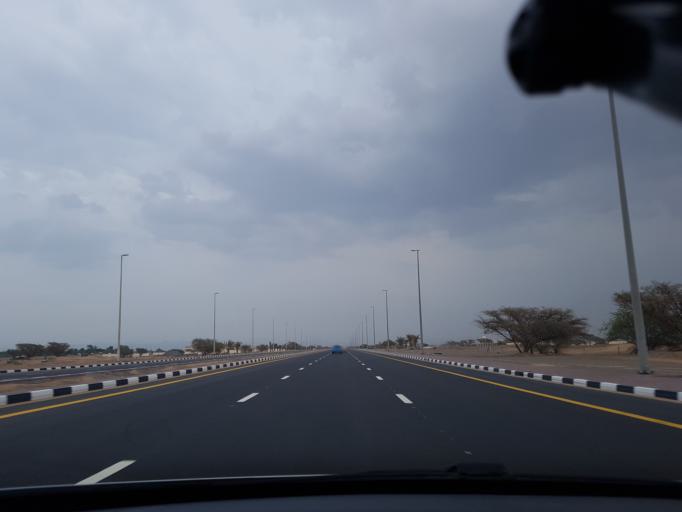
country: AE
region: Ash Shariqah
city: Adh Dhayd
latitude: 25.2675
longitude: 55.9033
